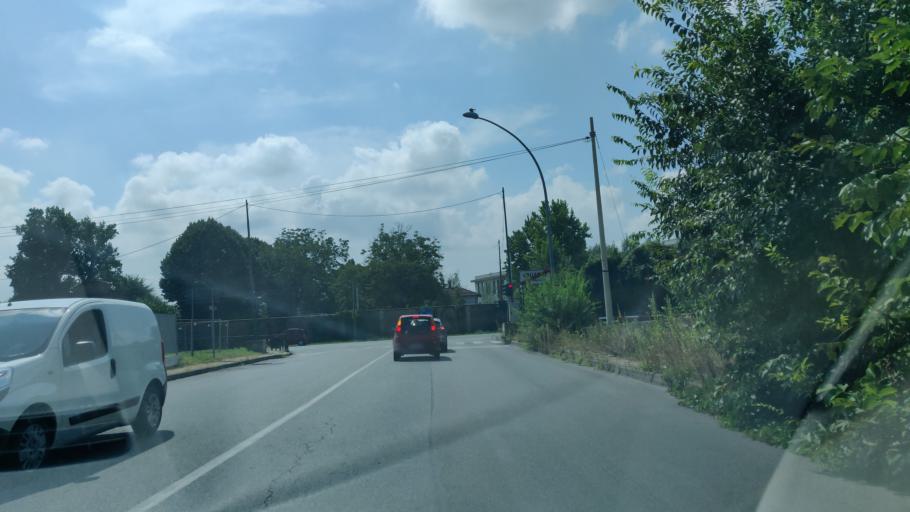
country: IT
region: Piedmont
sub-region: Provincia di Torino
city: Savonera
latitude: 45.0993
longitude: 7.6088
